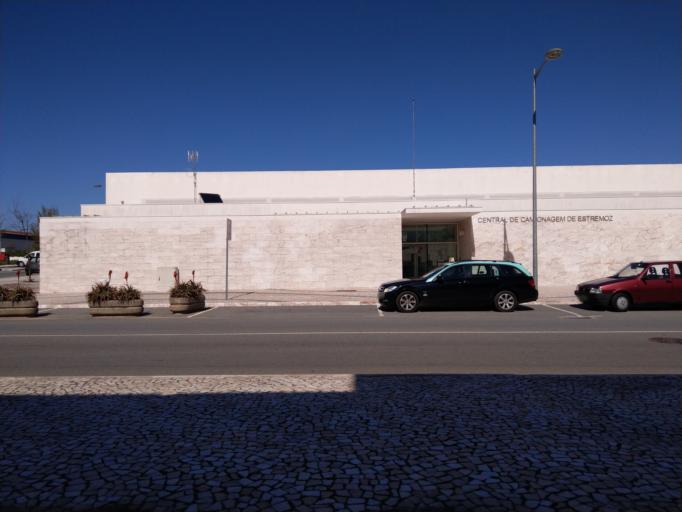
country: PT
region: Evora
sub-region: Estremoz
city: Estremoz
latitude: 38.8442
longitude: -7.5819
